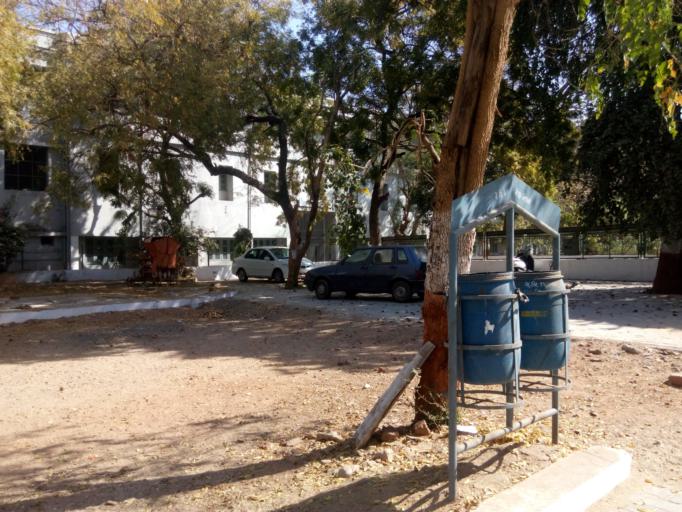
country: IN
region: Gujarat
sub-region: Ahmadabad
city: Ahmedabad
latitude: 23.0433
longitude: 72.5672
